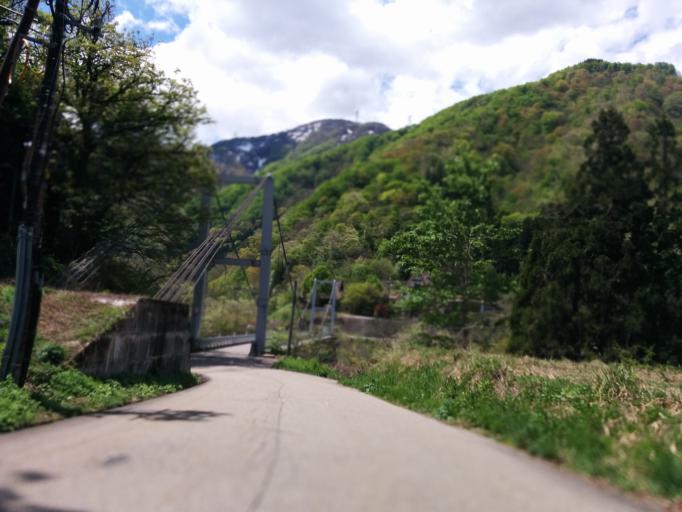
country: JP
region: Toyama
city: Fukumitsu
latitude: 36.4042
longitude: 136.8851
